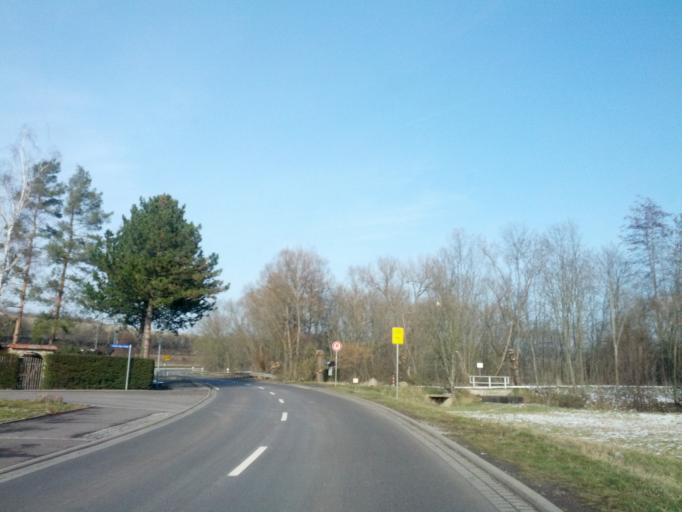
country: DE
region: Thuringia
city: Ingersleben
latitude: 50.9232
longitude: 10.9420
